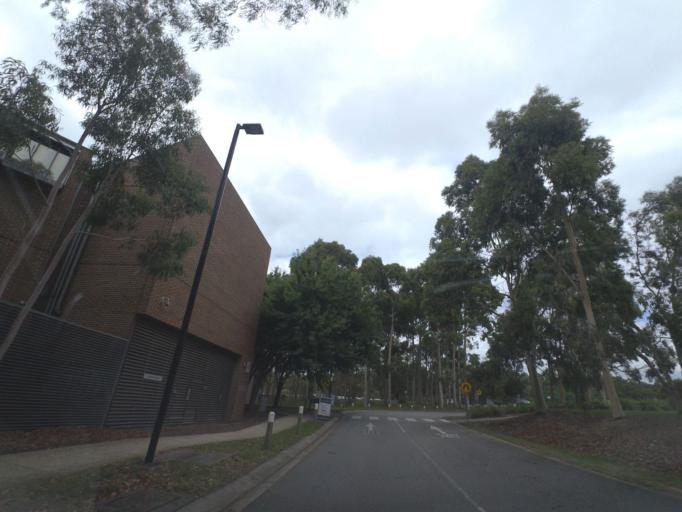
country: AU
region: Victoria
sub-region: Yarra Ranges
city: Lilydale
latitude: -37.7657
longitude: 145.3468
